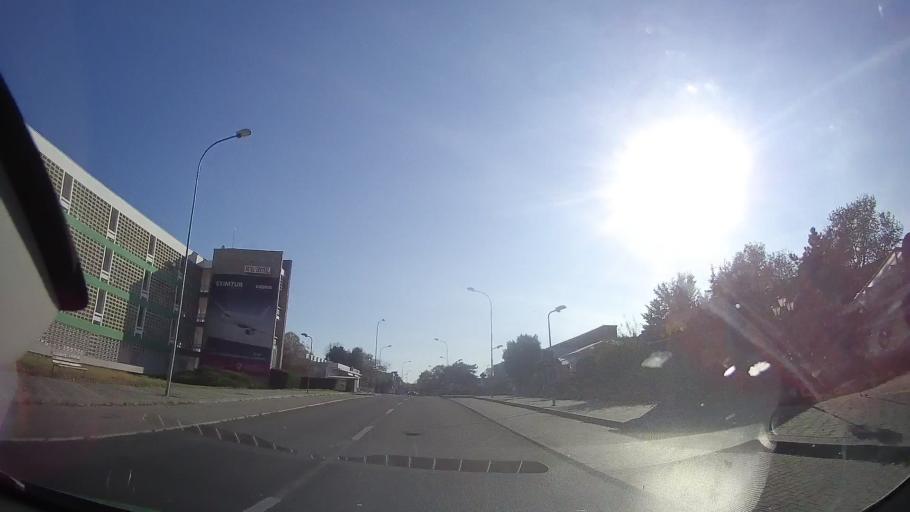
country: RO
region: Constanta
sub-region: Comuna Douazeci si Trei August
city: Douazeci si Trei August
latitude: 43.8678
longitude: 28.5974
